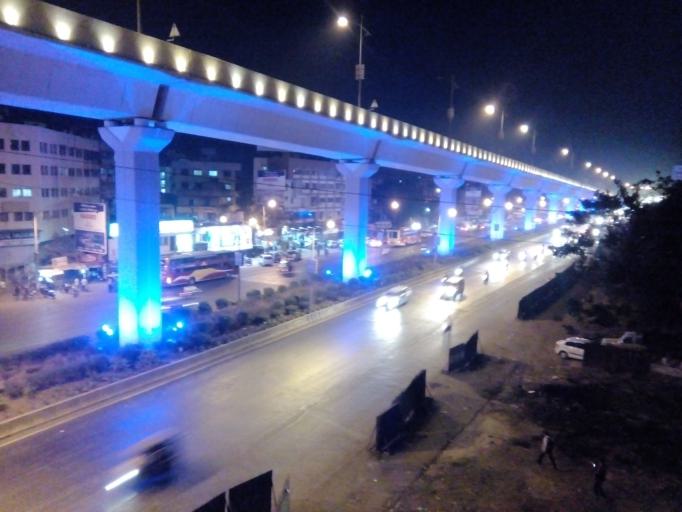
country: IN
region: Maharashtra
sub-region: Pune Division
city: Pimpri
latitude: 18.6066
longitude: 73.8222
